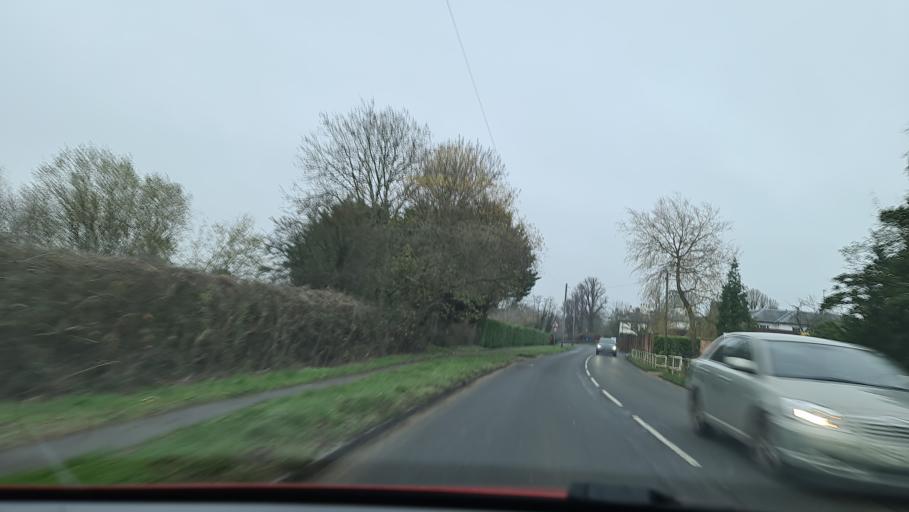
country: GB
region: England
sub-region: Buckinghamshire
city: Beaconsfield
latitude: 51.6316
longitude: -0.6804
